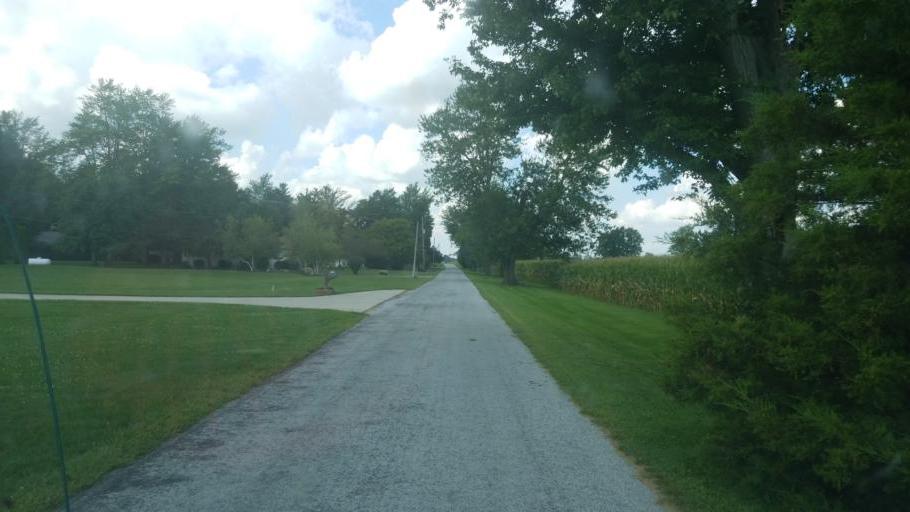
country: US
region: Ohio
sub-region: Hardin County
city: Kenton
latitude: 40.6879
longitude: -83.5634
